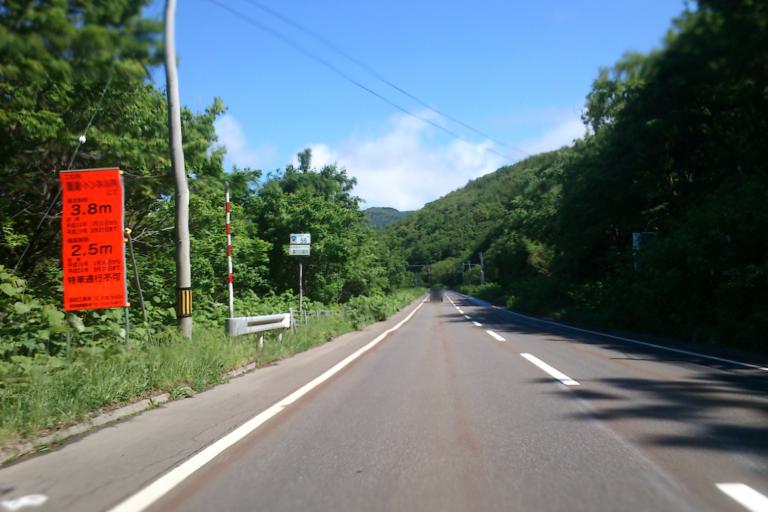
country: JP
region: Hokkaido
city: Ishikari
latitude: 43.4988
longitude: 141.3735
